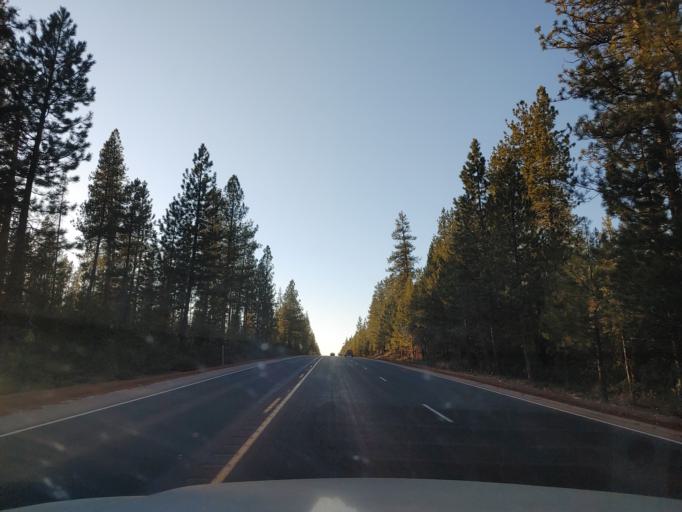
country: US
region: Oregon
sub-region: Deschutes County
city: La Pine
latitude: 43.4546
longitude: -121.8746
